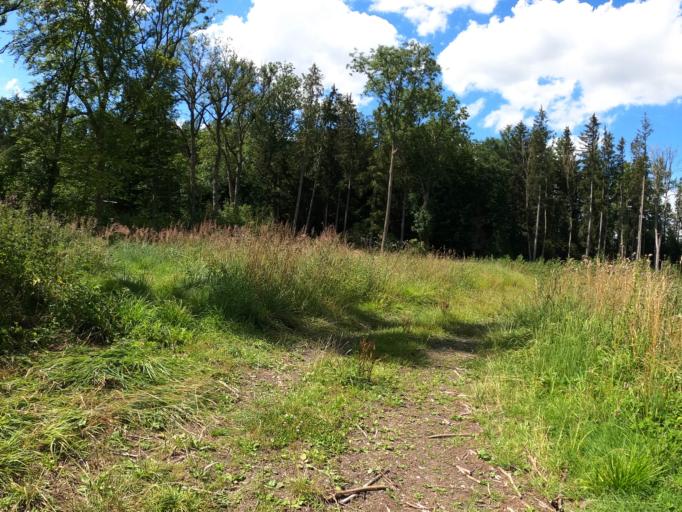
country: DE
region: Bavaria
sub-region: Swabia
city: Leipheim
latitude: 48.4101
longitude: 10.2147
